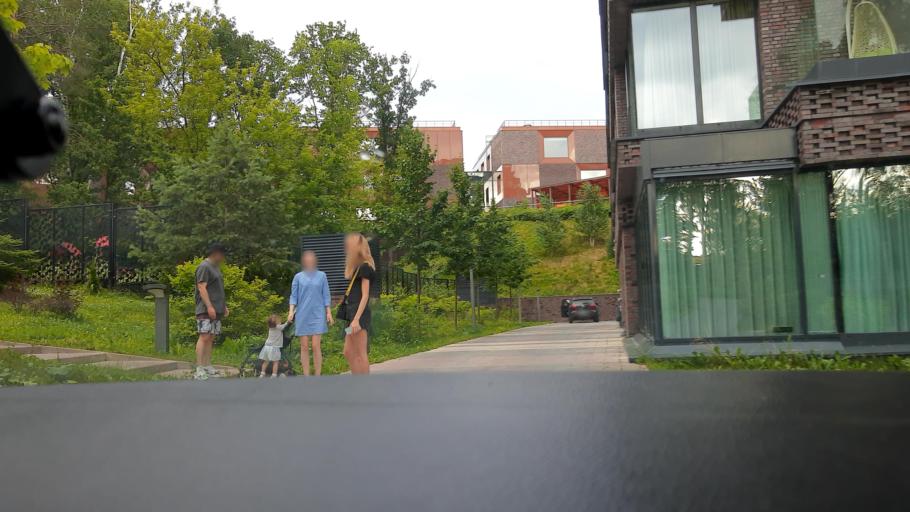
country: RU
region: Moskovskaya
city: Pavshino
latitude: 55.8123
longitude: 37.3789
